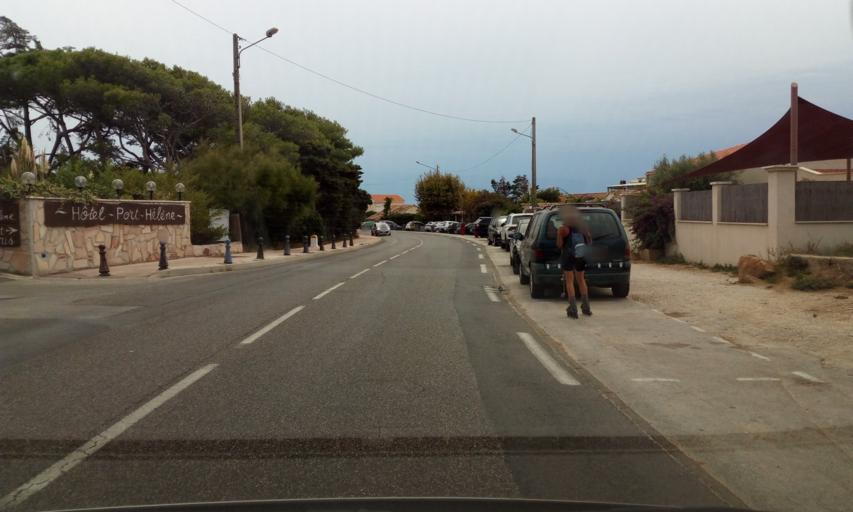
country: FR
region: Provence-Alpes-Cote d'Azur
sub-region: Departement du Var
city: Hyeres
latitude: 43.0821
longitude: 6.1185
